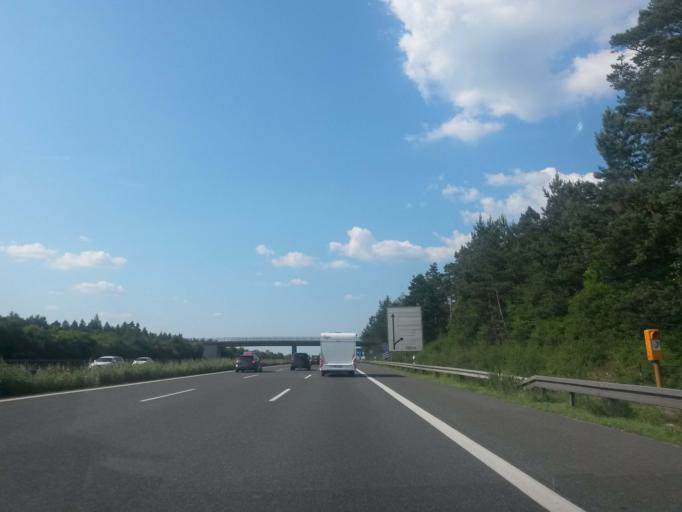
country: DE
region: Bavaria
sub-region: Regierungsbezirk Mittelfranken
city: Feucht
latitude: 49.3382
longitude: 11.2043
